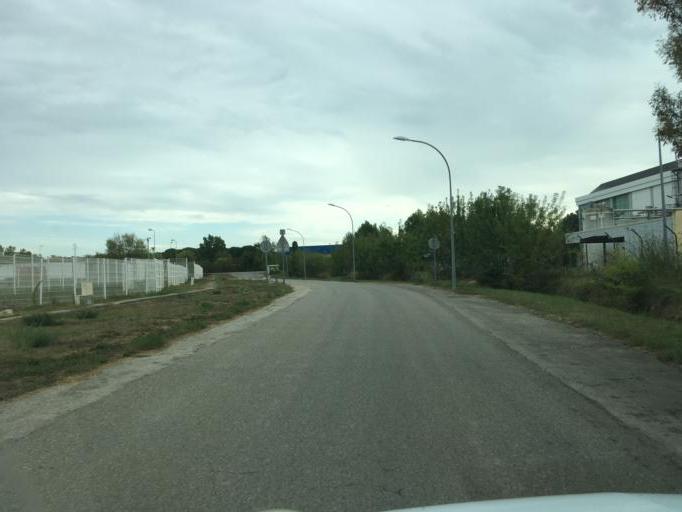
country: FR
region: Provence-Alpes-Cote d'Azur
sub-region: Departement des Bouches-du-Rhone
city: Rousset
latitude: 43.4726
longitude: 5.6016
